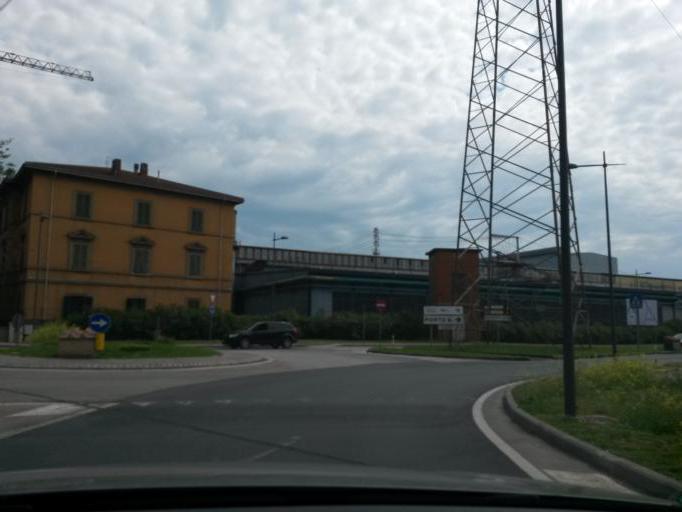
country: IT
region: Tuscany
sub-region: Provincia di Livorno
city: Piombino
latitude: 42.9281
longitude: 10.5328
